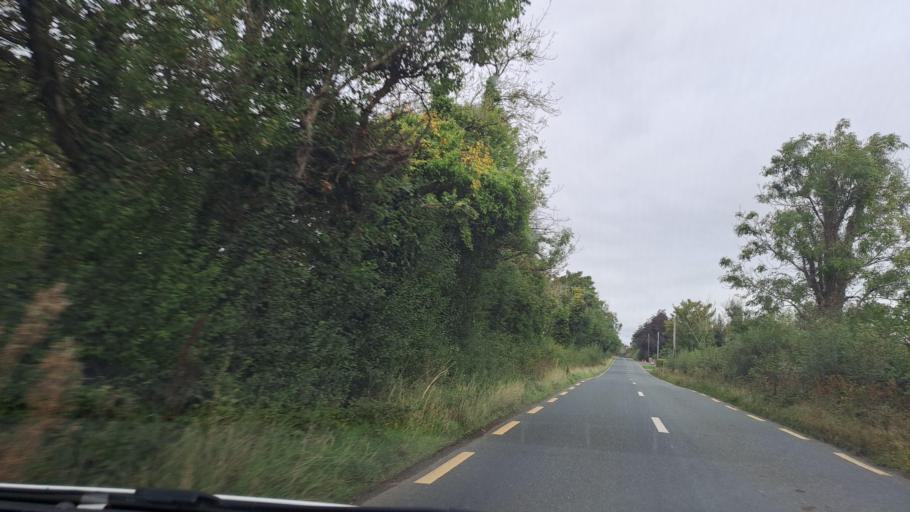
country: IE
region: Ulster
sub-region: An Cabhan
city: Kingscourt
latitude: 53.8915
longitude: -6.7558
